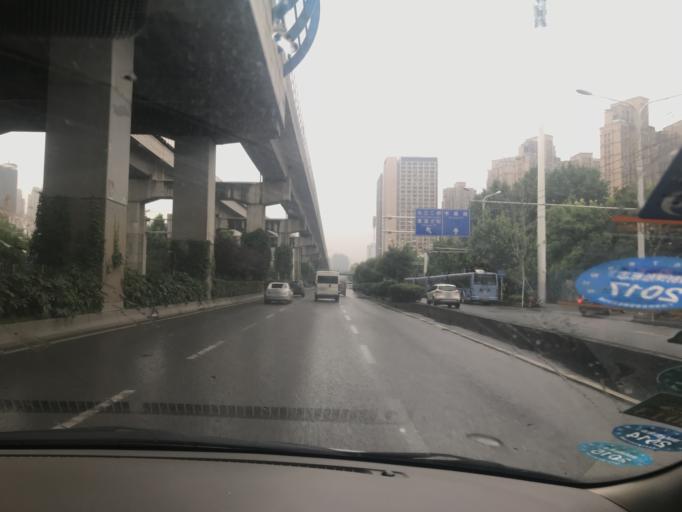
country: CN
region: Hubei
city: Jiang'an
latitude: 30.6276
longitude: 114.3132
